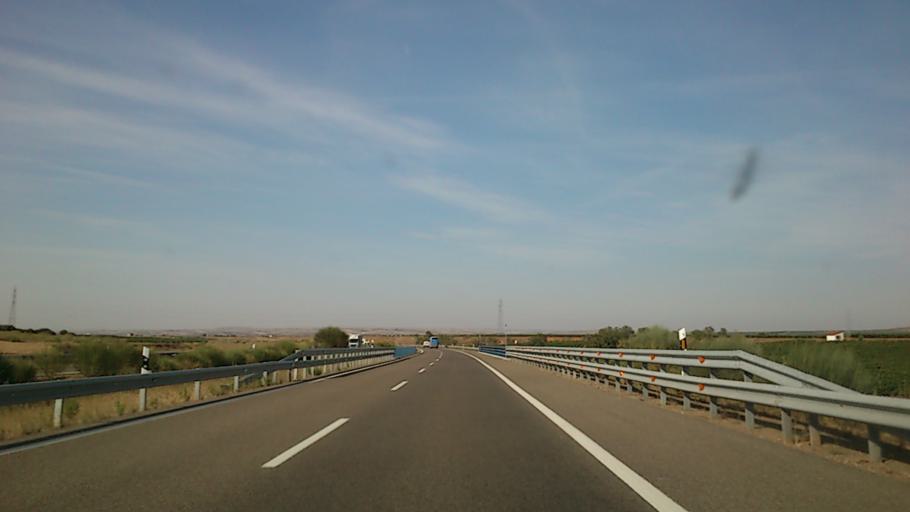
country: ES
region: Aragon
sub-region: Provincia de Zaragoza
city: Carinena
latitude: 41.3212
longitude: -1.2050
